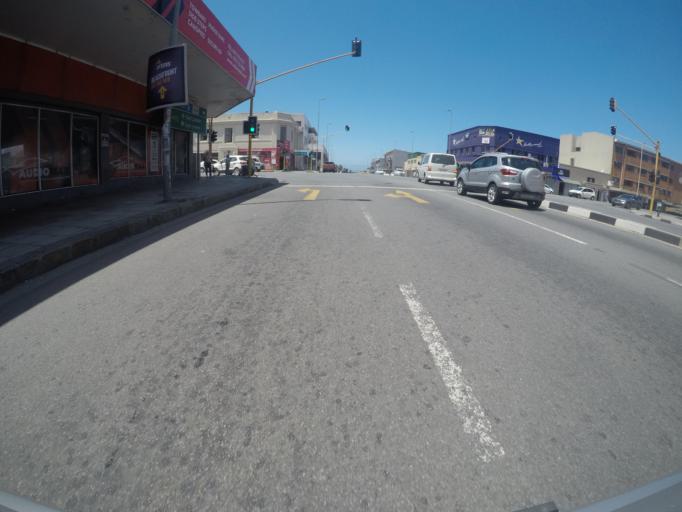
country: ZA
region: Eastern Cape
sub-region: Buffalo City Metropolitan Municipality
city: East London
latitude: -33.0176
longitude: 27.9127
